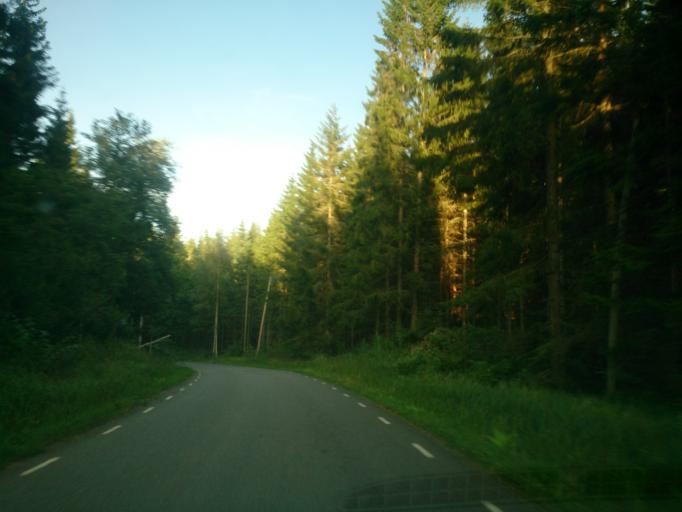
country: SE
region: OEstergoetland
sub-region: Atvidabergs Kommun
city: Atvidaberg
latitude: 58.2759
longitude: 16.1323
